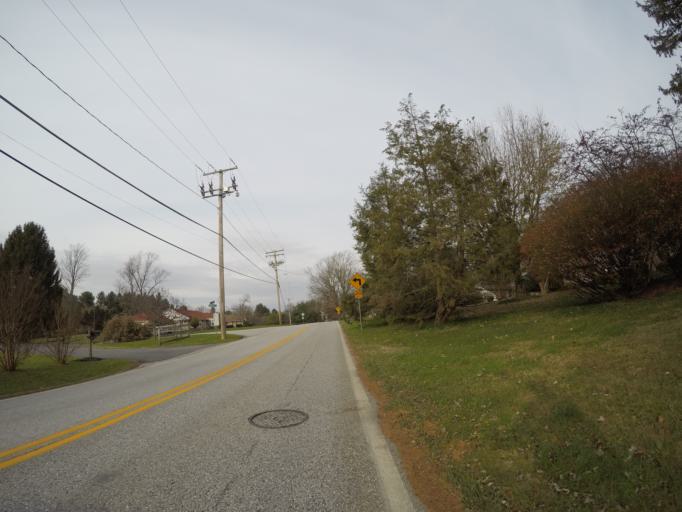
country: US
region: Maryland
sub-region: Howard County
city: Columbia
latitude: 39.2605
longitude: -76.8245
